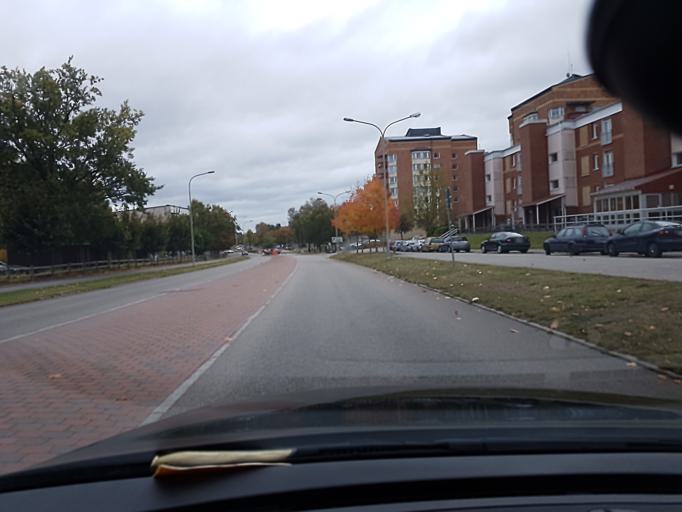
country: SE
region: Kronoberg
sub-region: Vaxjo Kommun
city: Vaexjoe
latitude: 56.8920
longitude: 14.7988
